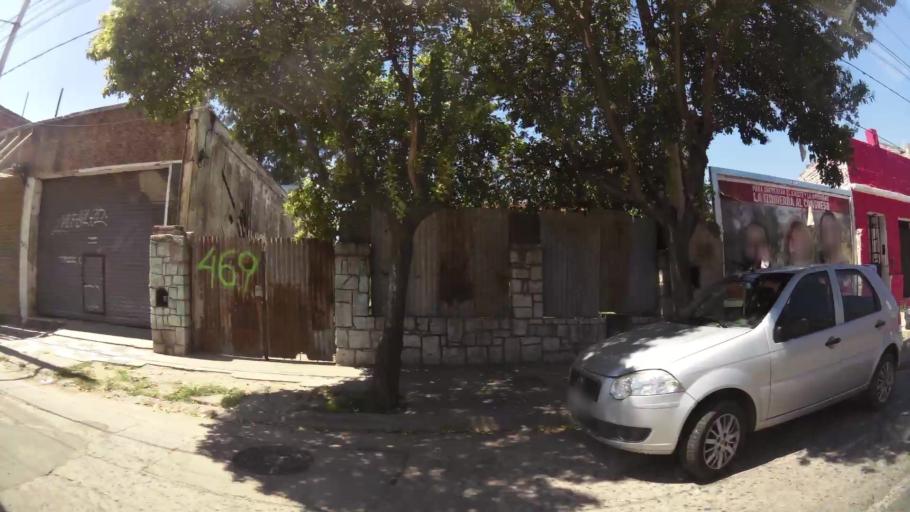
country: AR
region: Cordoba
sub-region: Departamento de Capital
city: Cordoba
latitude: -31.4281
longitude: -64.1967
